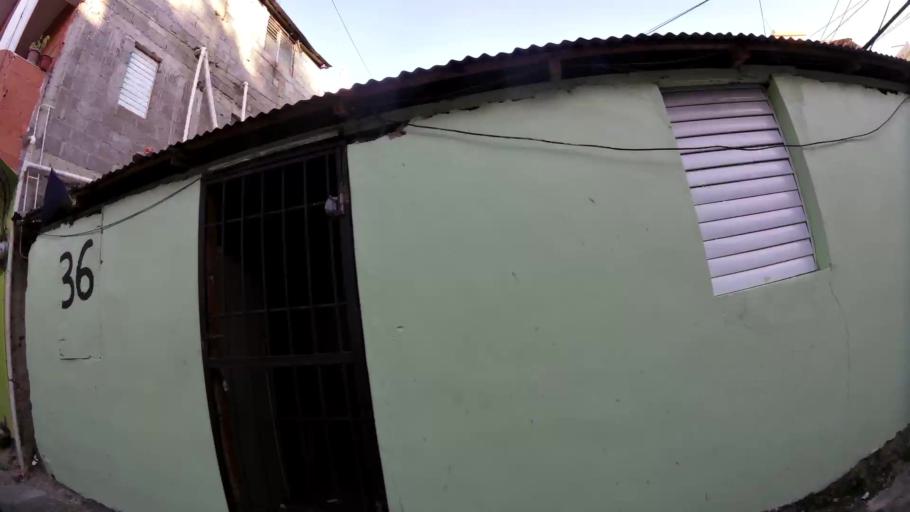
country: DO
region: Nacional
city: Santo Domingo
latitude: 18.4890
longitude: -69.9681
